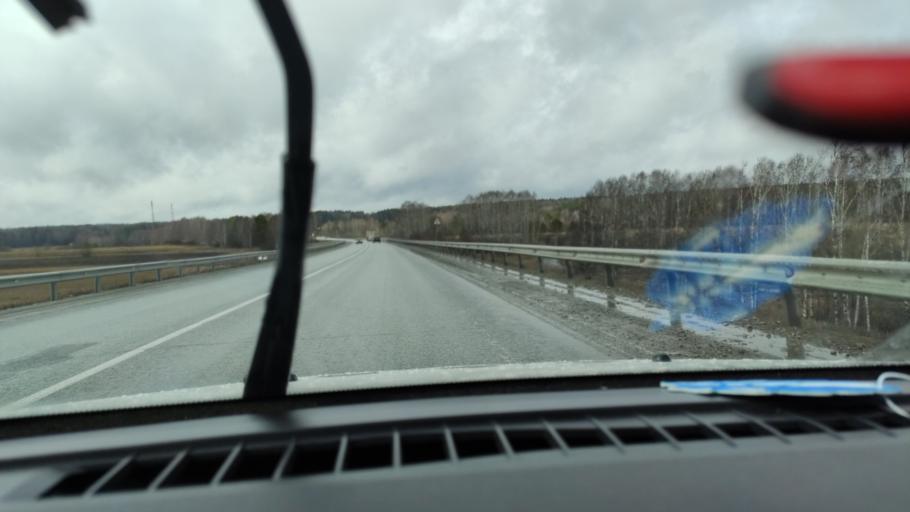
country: RU
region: Sverdlovsk
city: Druzhinino
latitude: 56.8106
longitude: 59.5102
